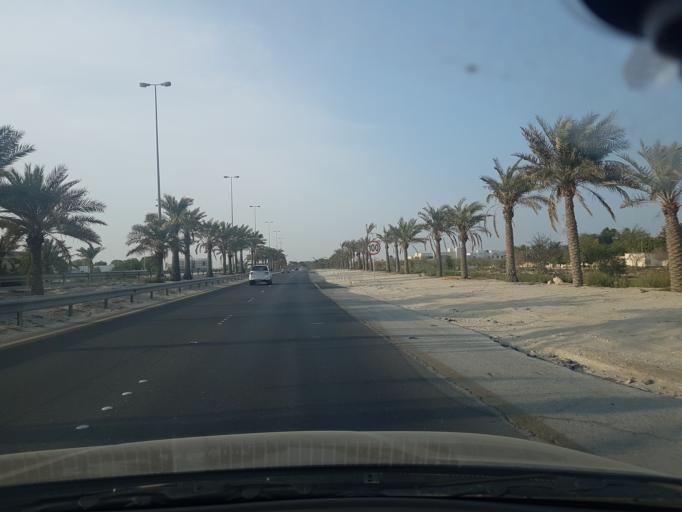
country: BH
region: Northern
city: Ar Rifa'
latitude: 26.1378
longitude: 50.5388
